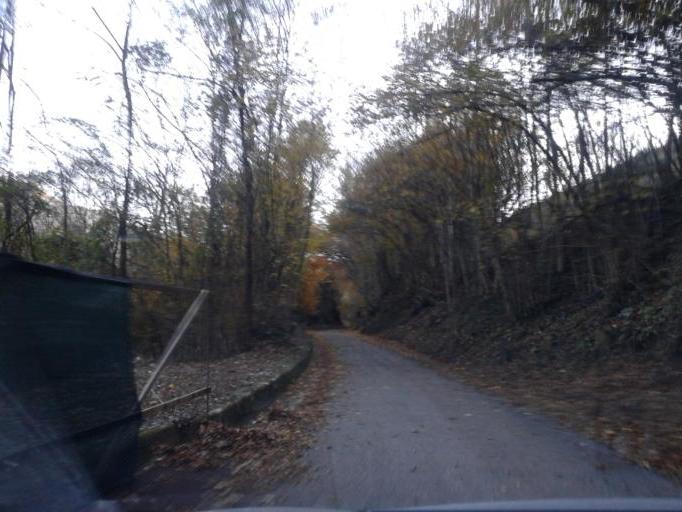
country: IT
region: Trentino-Alto Adige
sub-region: Provincia di Trento
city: Pieve di Ledro
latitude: 45.8999
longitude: 10.7038
